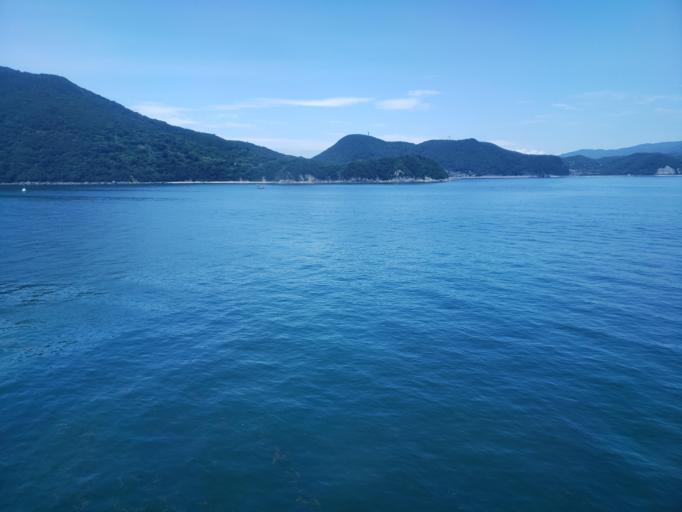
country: JP
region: Kagawa
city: Tonosho
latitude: 34.4143
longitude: 134.2558
